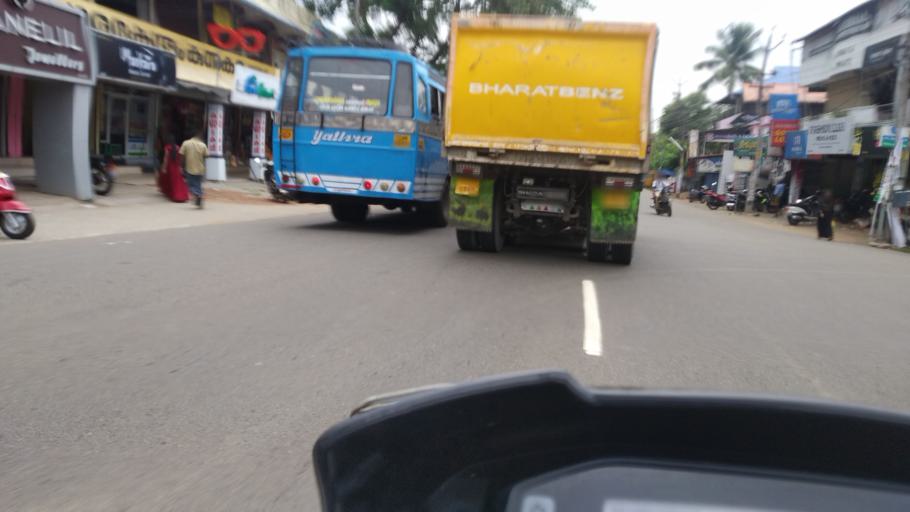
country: IN
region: Kerala
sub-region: Ernakulam
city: Aluva
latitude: 10.1552
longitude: 76.2953
